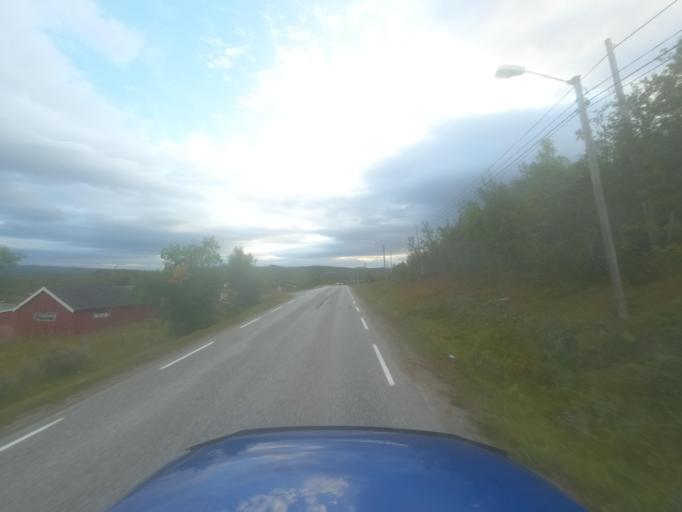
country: NO
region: Finnmark Fylke
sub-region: Porsanger
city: Lakselv
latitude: 70.5068
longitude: 25.0525
